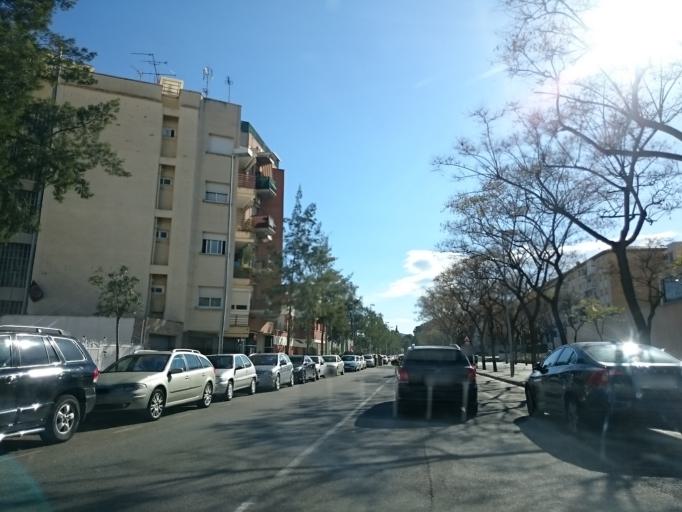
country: ES
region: Catalonia
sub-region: Provincia de Barcelona
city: Gava
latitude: 41.3094
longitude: 1.9932
